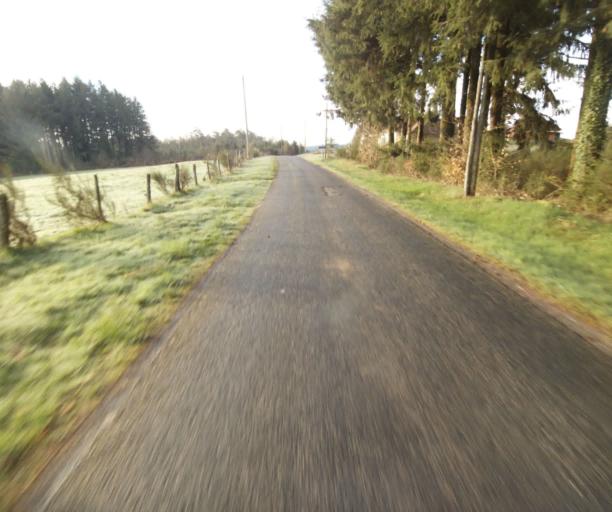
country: FR
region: Limousin
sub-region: Departement de la Correze
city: Correze
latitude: 45.3232
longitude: 1.8652
